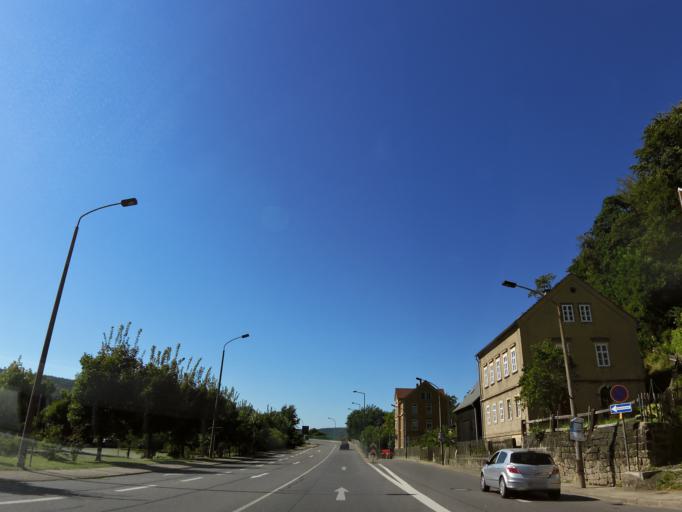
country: DE
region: Saxony
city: Rathmannsdorf
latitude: 50.9221
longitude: 14.1400
